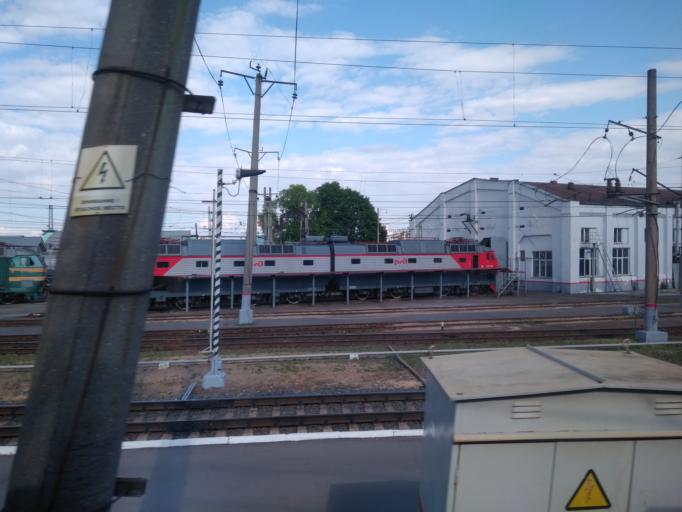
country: RU
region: Moscow
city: Mar'ina Roshcha
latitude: 55.7882
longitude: 37.6423
